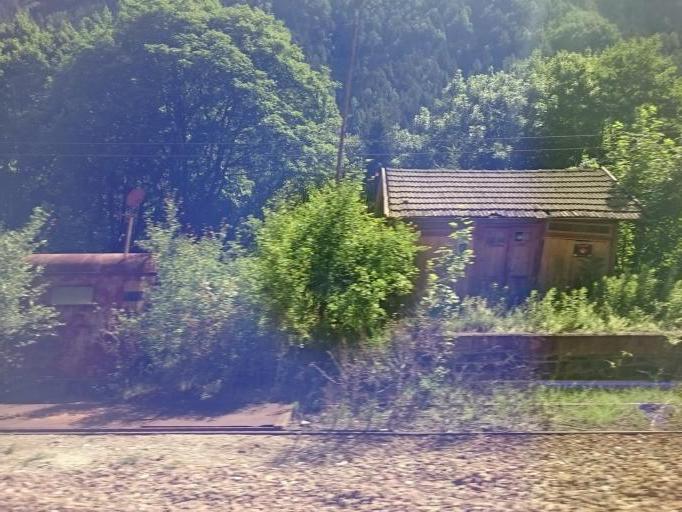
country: IT
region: Trentino-Alto Adige
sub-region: Bolzano
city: Campo di Trens
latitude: 46.8203
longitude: 11.5368
